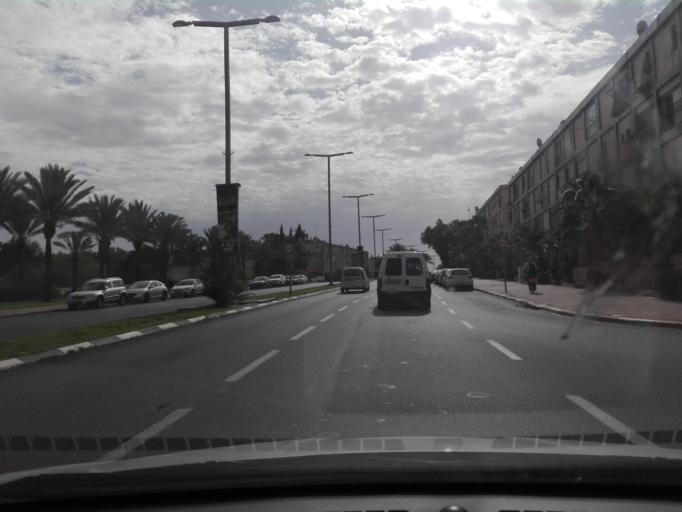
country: IL
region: Southern District
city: Beersheba
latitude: 31.2730
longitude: 34.7977
